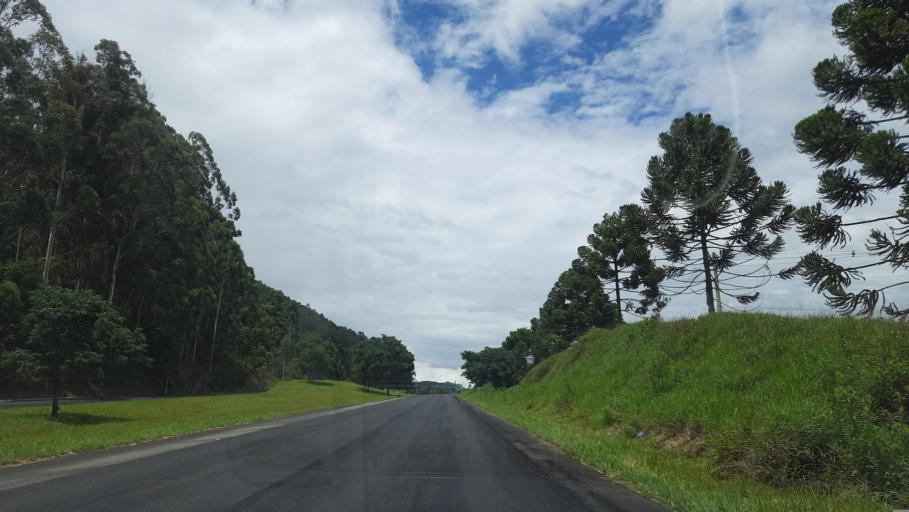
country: BR
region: Minas Gerais
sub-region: Pocos De Caldas
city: Pocos de Caldas
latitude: -21.8017
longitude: -46.6501
